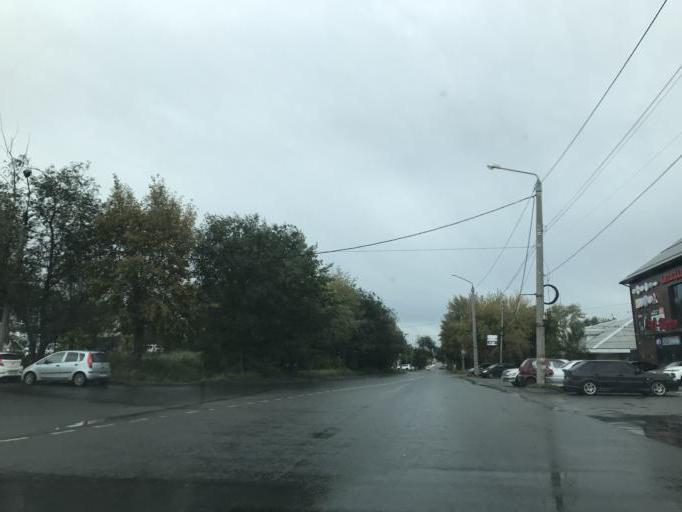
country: RU
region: Chelyabinsk
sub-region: Gorod Chelyabinsk
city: Chelyabinsk
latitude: 55.1913
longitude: 61.4239
